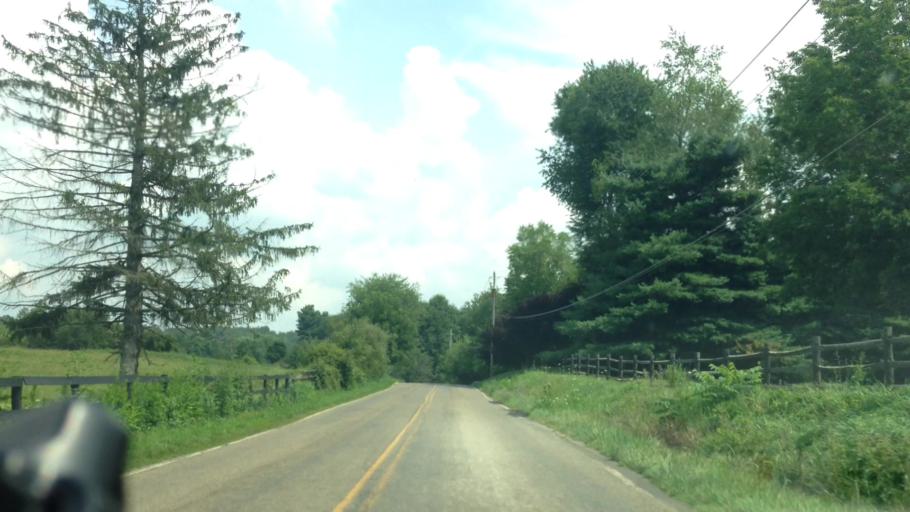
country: US
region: Ohio
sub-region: Stark County
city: Canal Fulton
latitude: 40.8637
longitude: -81.5609
